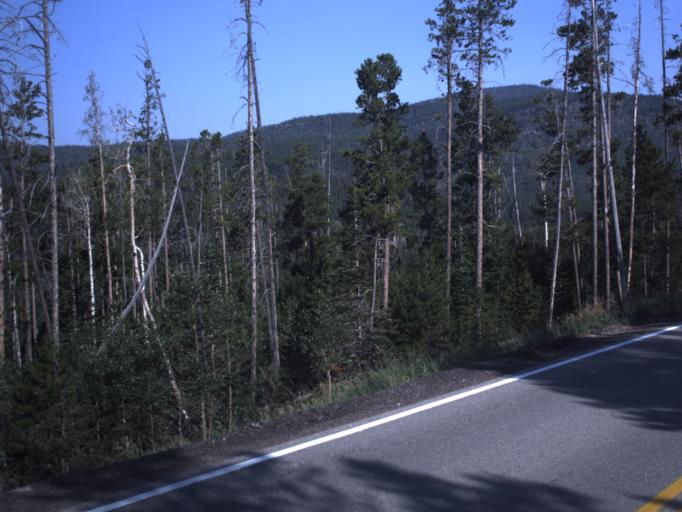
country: US
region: Utah
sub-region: Uintah County
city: Maeser
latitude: 40.7583
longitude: -109.4707
